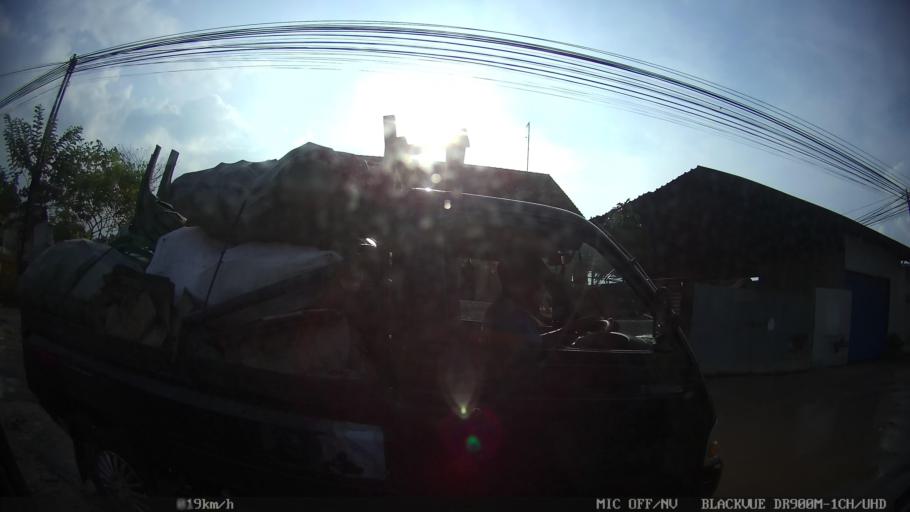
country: ID
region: Lampung
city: Kedaton
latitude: -5.3873
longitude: 105.3153
